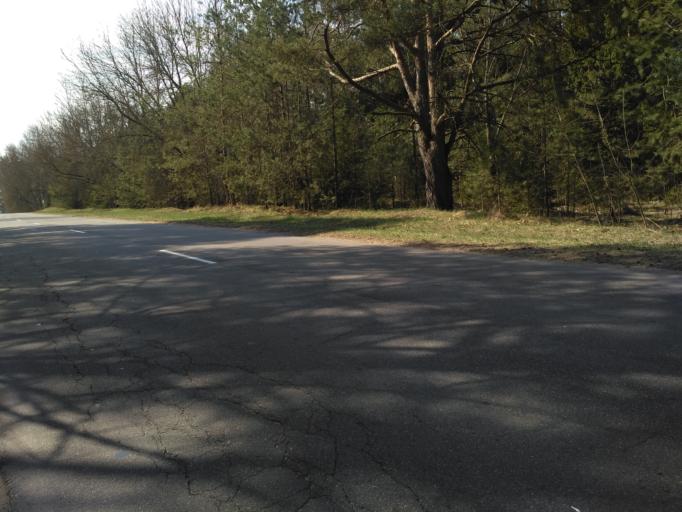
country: BY
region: Minsk
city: Zamostochcha
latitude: 53.8964
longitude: 27.9281
